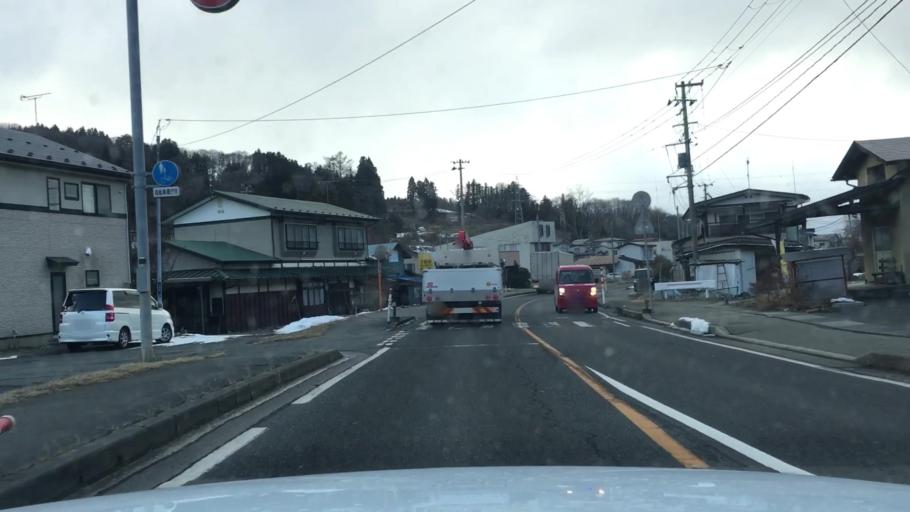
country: JP
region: Iwate
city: Morioka-shi
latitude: 39.6811
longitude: 141.1840
